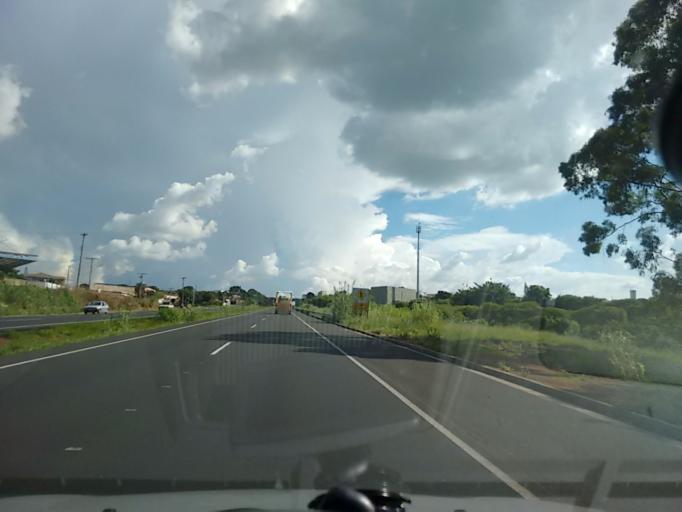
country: BR
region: Sao Paulo
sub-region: Marilia
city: Marilia
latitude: -22.2180
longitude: -49.9655
